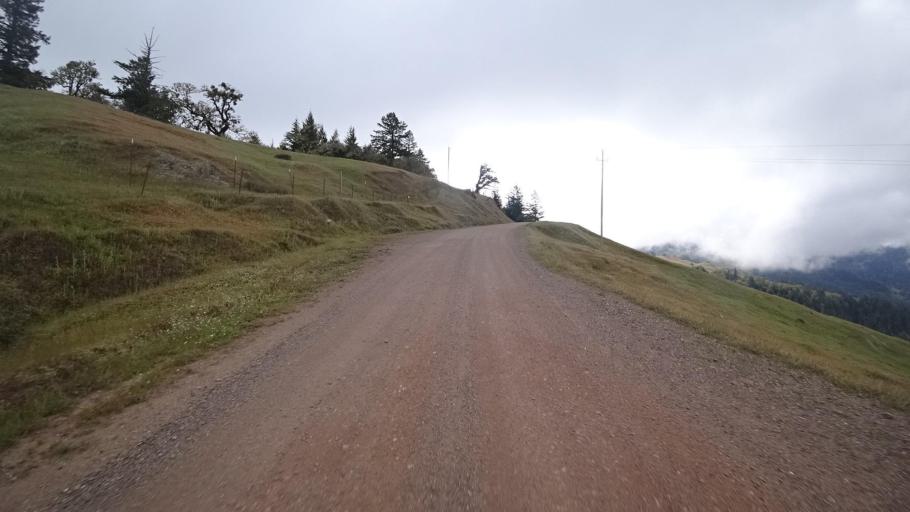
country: US
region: California
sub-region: Humboldt County
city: Redway
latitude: 40.2130
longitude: -123.7400
